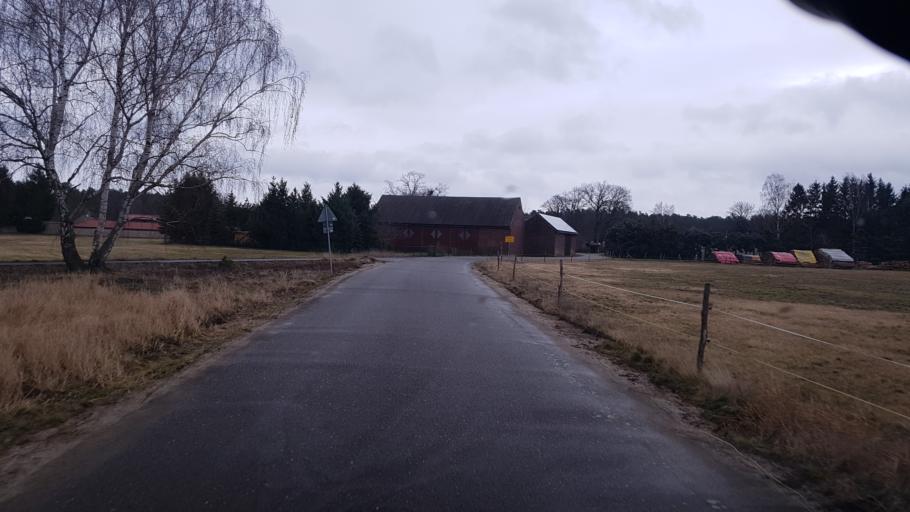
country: DE
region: Brandenburg
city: Sallgast
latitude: 51.6660
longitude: 13.8226
